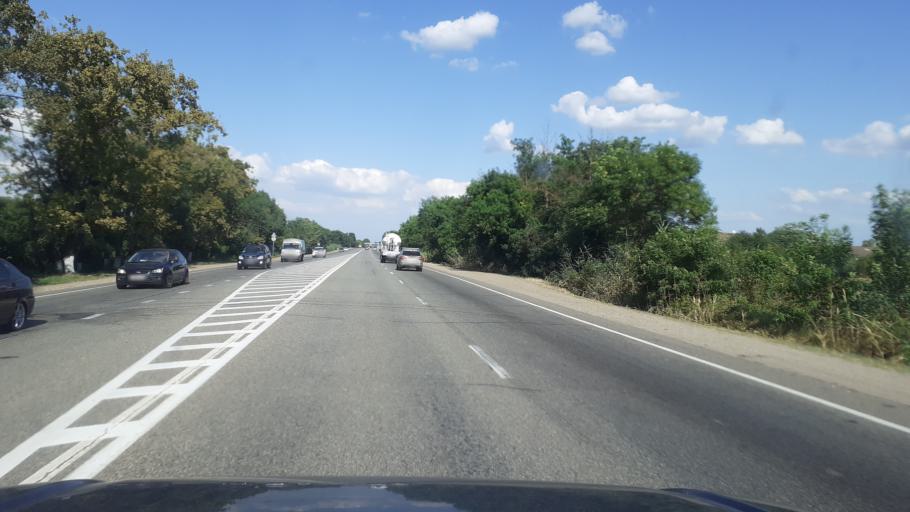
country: RU
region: Krasnodarskiy
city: Afipskiy
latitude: 44.8836
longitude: 38.7923
